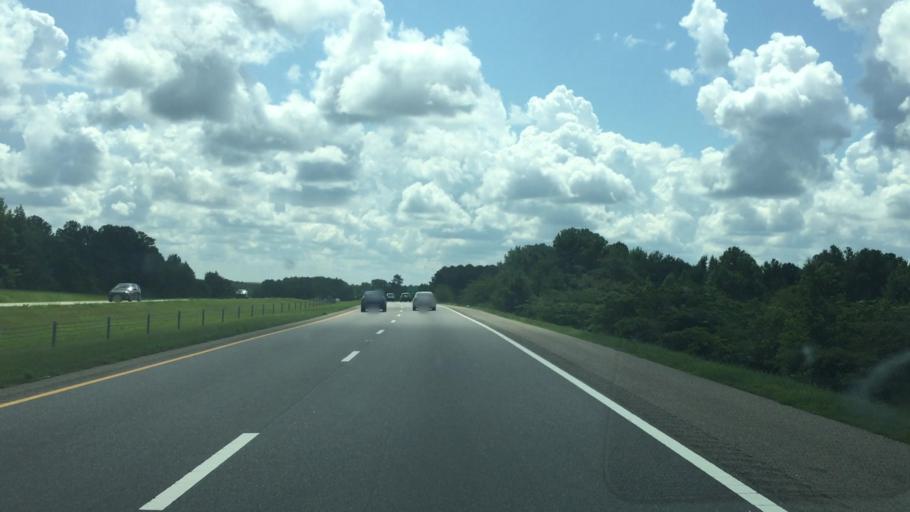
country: US
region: North Carolina
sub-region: Richmond County
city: Cordova
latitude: 34.9355
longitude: -79.8389
